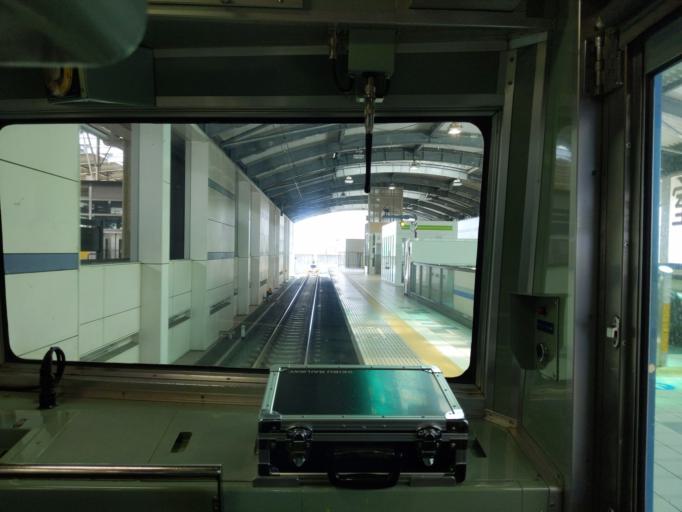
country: JP
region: Tokyo
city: Kamirenjaku
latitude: 35.7018
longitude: 139.5437
